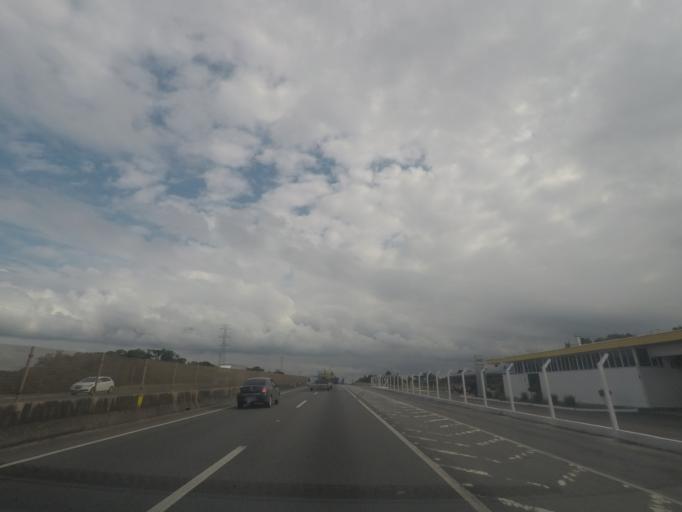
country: BR
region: Parana
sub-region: Piraquara
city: Piraquara
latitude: -25.4925
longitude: -49.1142
